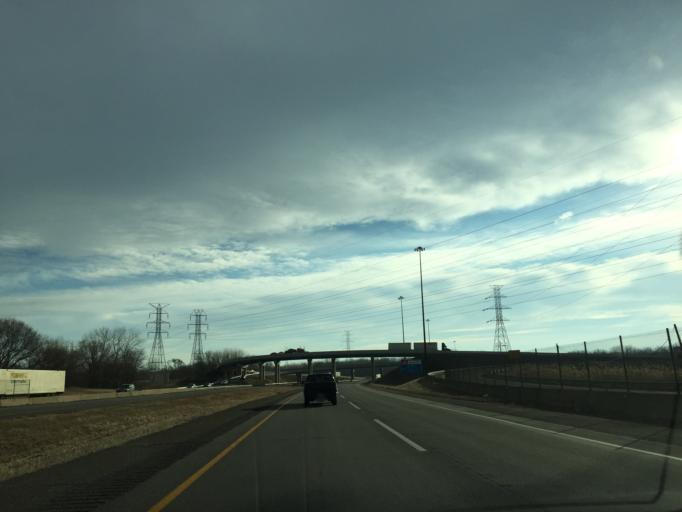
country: US
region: Indiana
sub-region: Lake County
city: Lake Station
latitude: 41.5930
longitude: -87.2366
